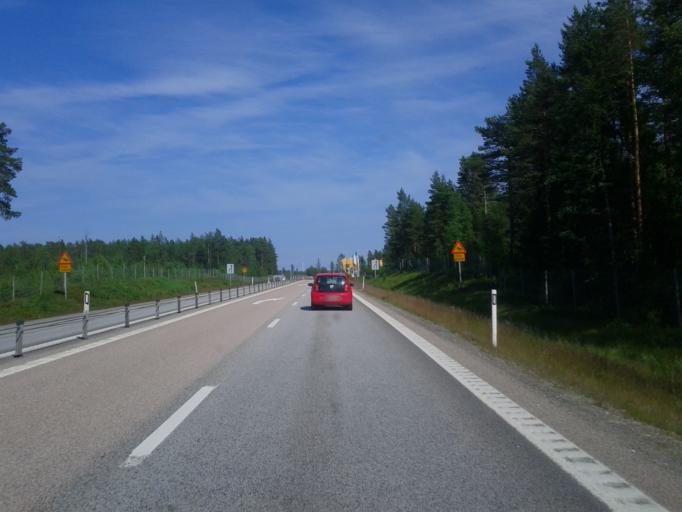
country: SE
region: Vaesterbotten
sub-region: Umea Kommun
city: Hoernefors
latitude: 63.6288
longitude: 19.8698
